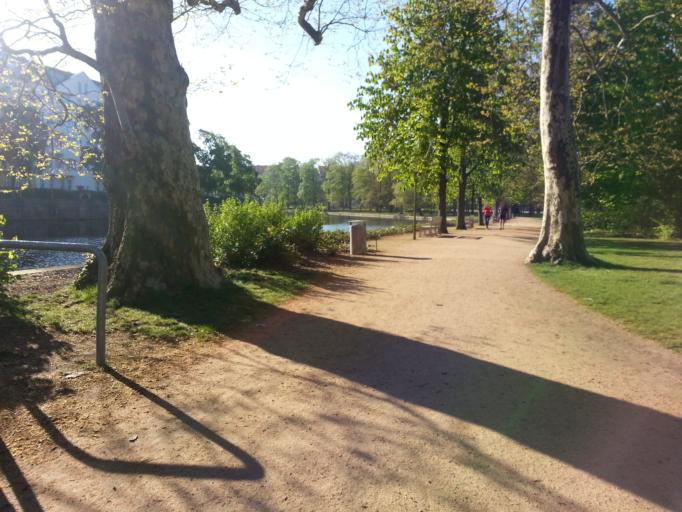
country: DE
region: Berlin
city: Charlottenburg-Nord
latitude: 52.5235
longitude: 13.2966
